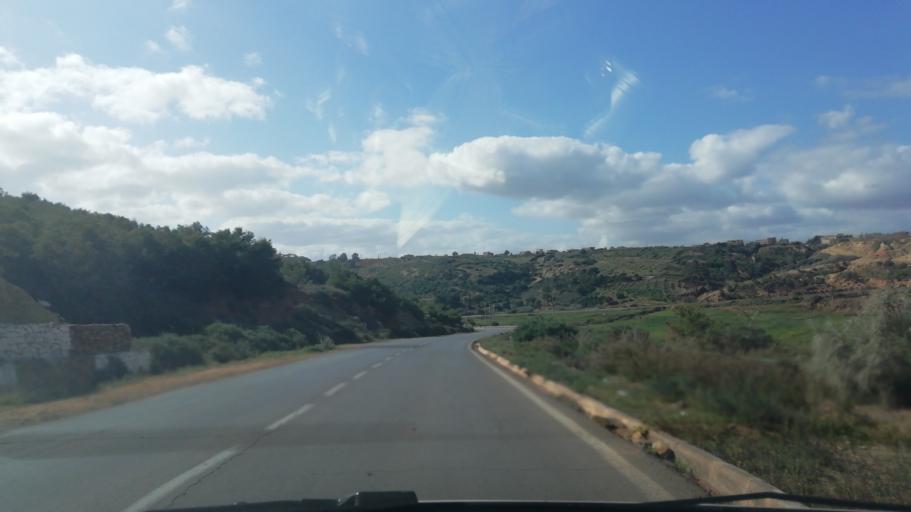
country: DZ
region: Relizane
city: Mazouna
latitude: 36.3211
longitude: 0.6854
